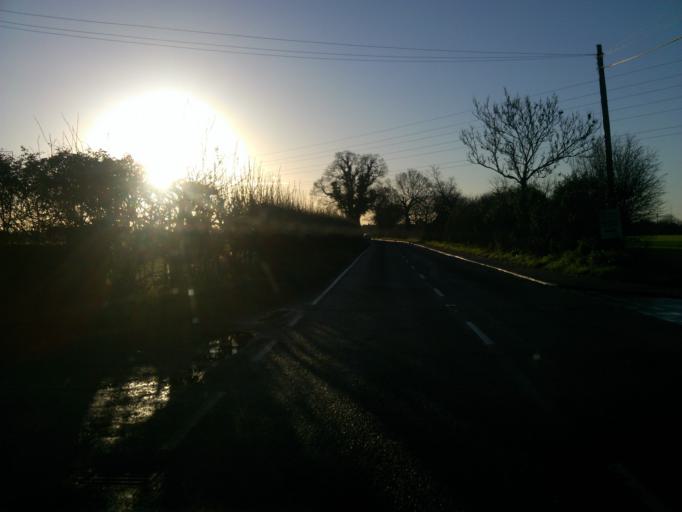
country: GB
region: England
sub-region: Essex
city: Alresford
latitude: 51.8617
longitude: 0.9964
